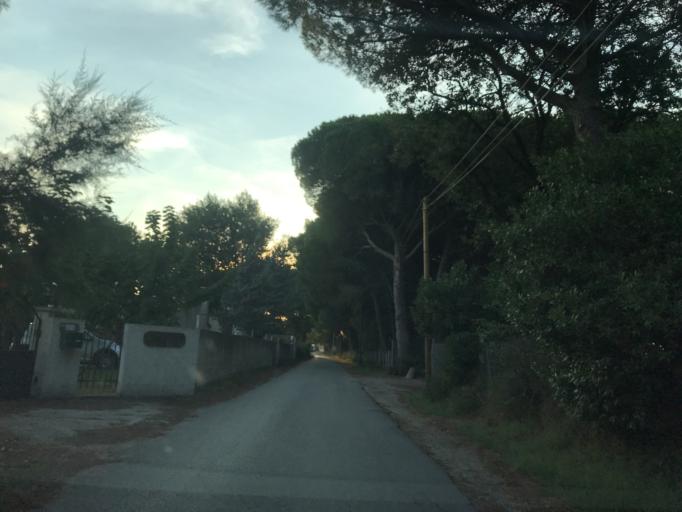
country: FR
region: Languedoc-Roussillon
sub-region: Departement du Gard
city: Aigues-Mortes
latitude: 43.5830
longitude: 4.2045
